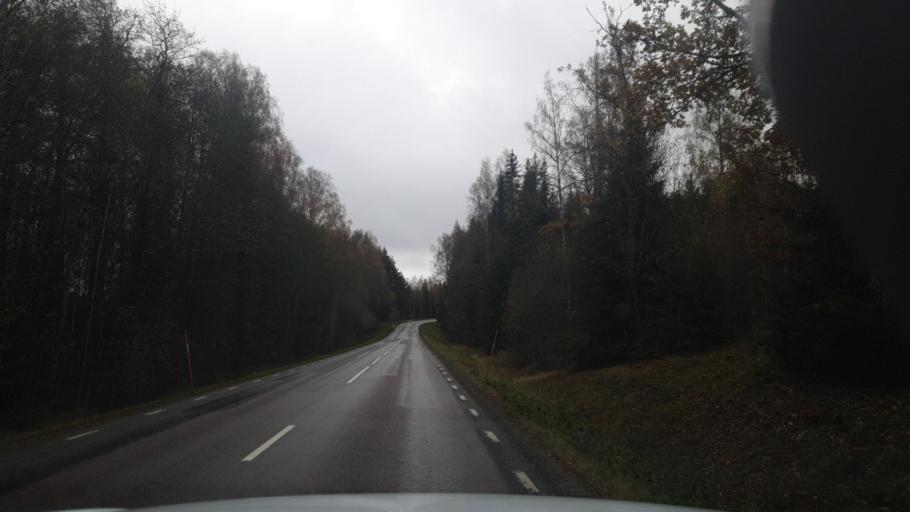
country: SE
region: Vaermland
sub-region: Eda Kommun
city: Charlottenberg
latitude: 59.7910
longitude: 12.2564
